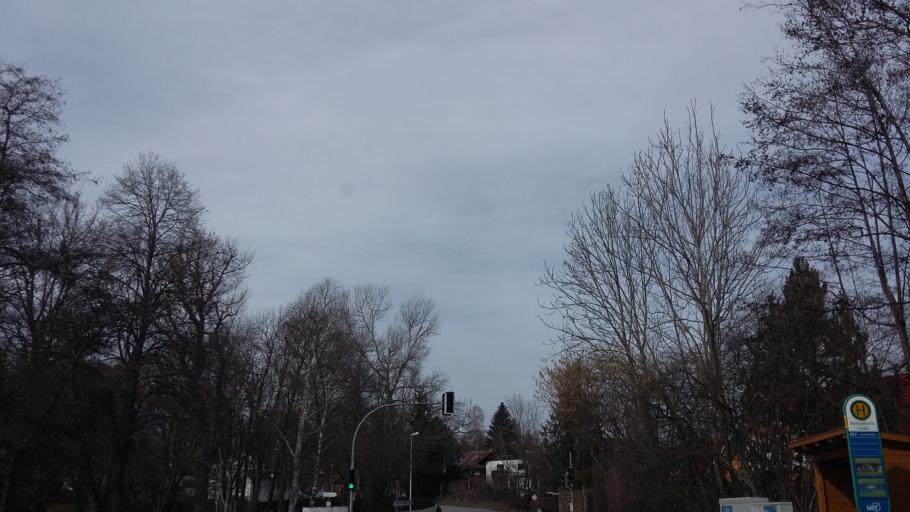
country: DE
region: Bavaria
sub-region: Upper Bavaria
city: Herrsching am Ammersee
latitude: 48.0044
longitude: 11.1652
